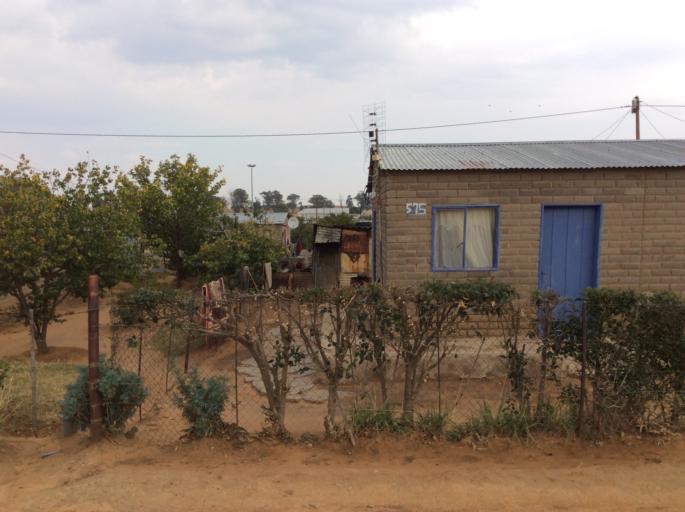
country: LS
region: Mafeteng
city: Mafeteng
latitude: -29.9855
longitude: 27.0101
